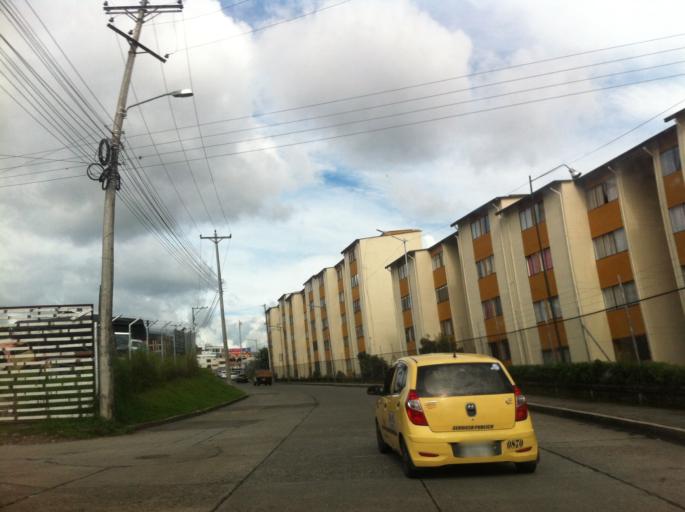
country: CO
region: Quindio
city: Armenia
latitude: 4.5309
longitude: -75.6785
